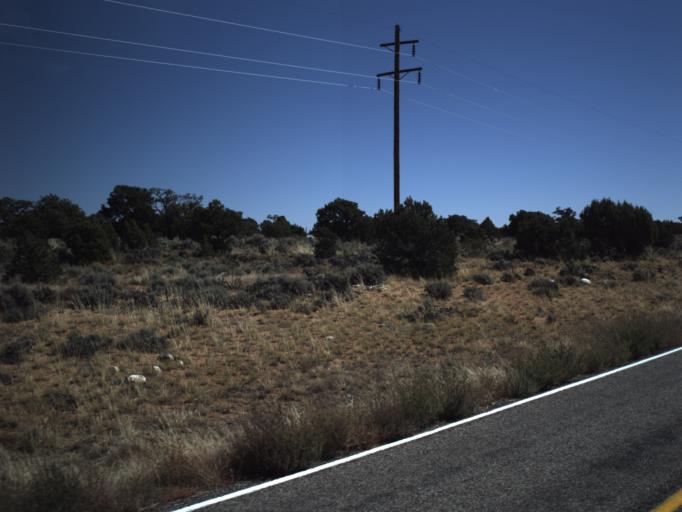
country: US
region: Utah
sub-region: Wayne County
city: Loa
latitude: 37.8532
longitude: -111.4317
